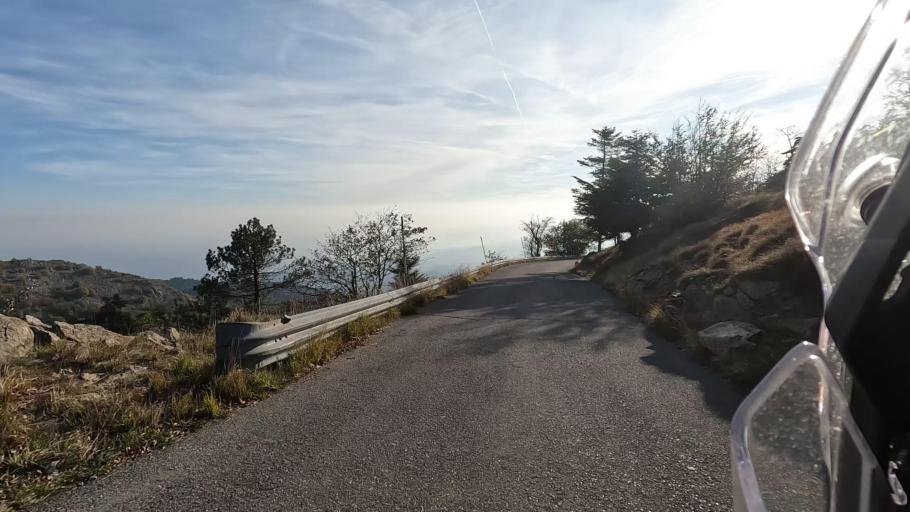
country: IT
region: Liguria
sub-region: Provincia di Savona
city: San Giovanni
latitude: 44.4290
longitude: 8.5492
